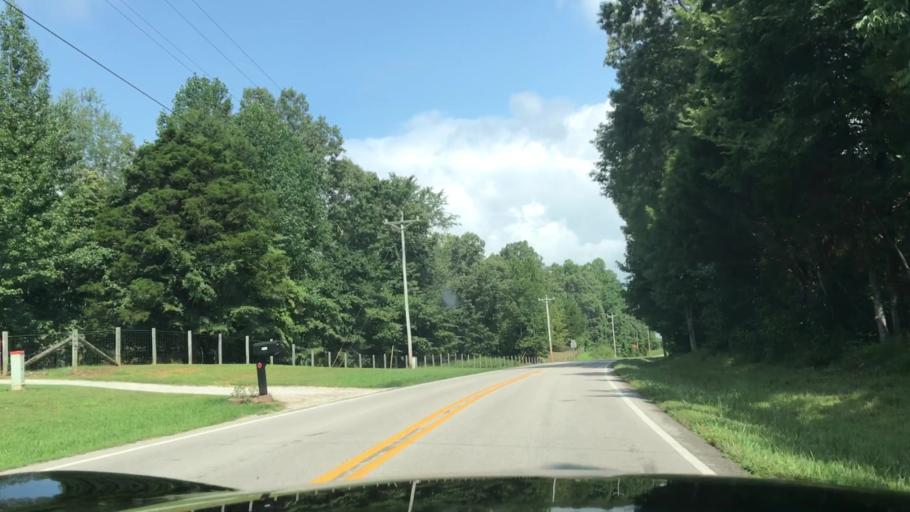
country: US
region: Kentucky
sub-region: Butler County
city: Morgantown
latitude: 37.1856
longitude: -86.8766
